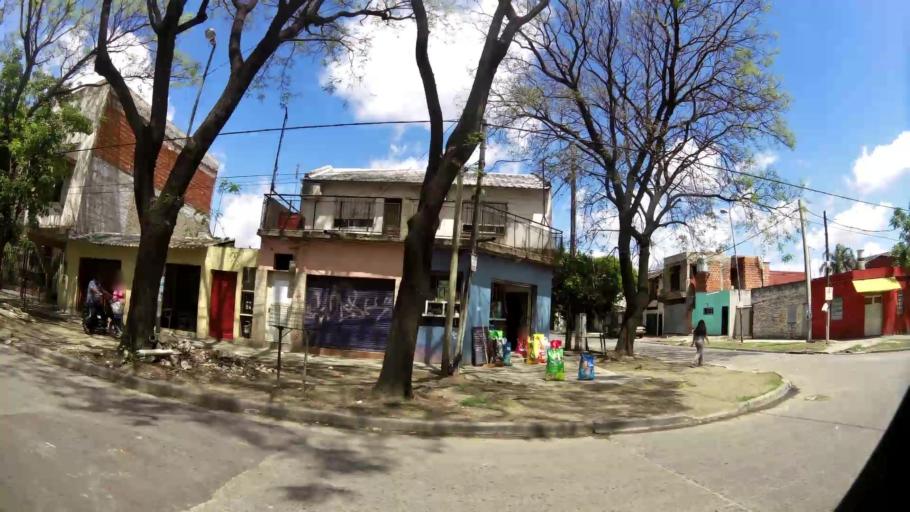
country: AR
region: Buenos Aires
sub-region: Partido de Lanus
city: Lanus
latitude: -34.6969
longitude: -58.4314
